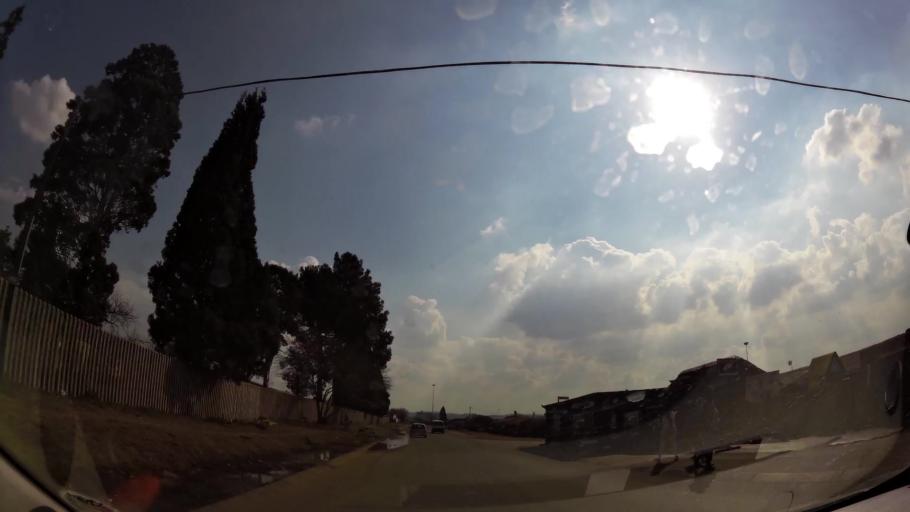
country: ZA
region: Gauteng
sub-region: Ekurhuleni Metropolitan Municipality
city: Germiston
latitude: -26.3096
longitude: 28.1520
